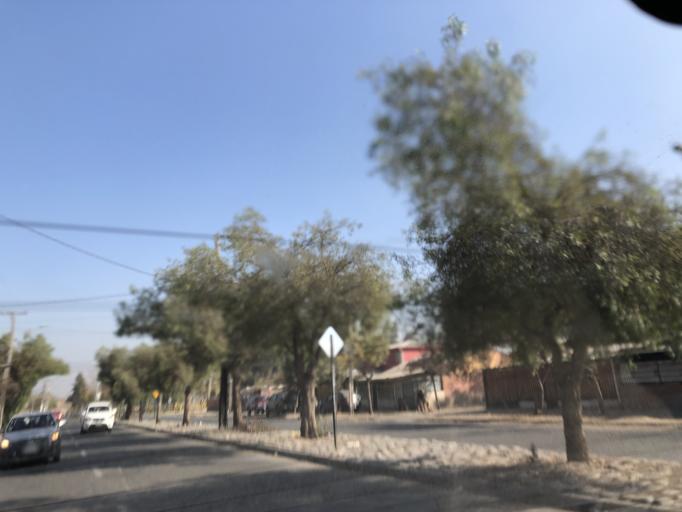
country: CL
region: Santiago Metropolitan
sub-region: Provincia de Cordillera
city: Puente Alto
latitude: -33.6192
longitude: -70.5940
